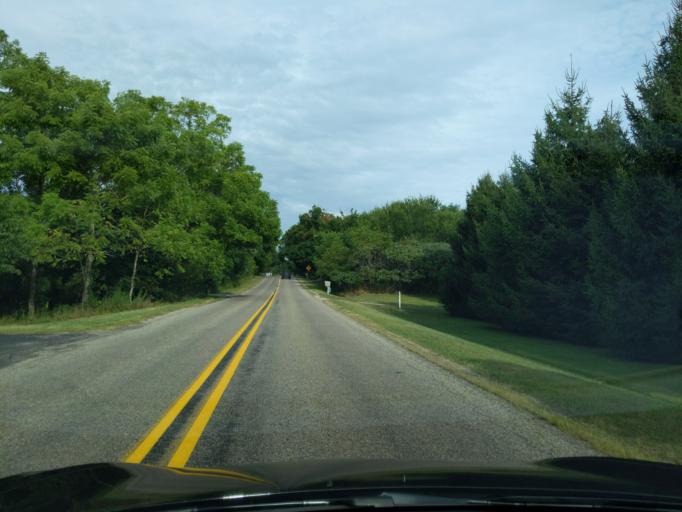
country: US
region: Michigan
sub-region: Eaton County
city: Dimondale
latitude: 42.6692
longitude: -84.6273
